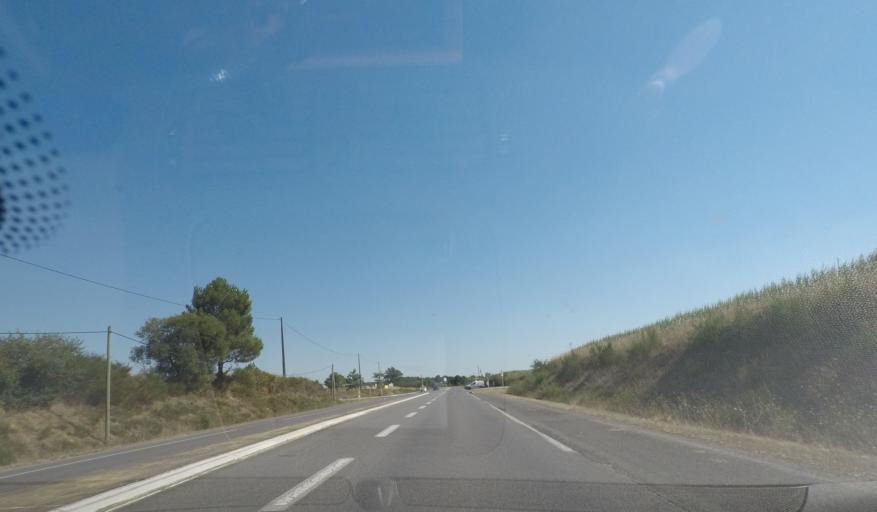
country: FR
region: Brittany
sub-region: Departement du Morbihan
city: Limerzel
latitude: 47.6227
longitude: -2.4068
